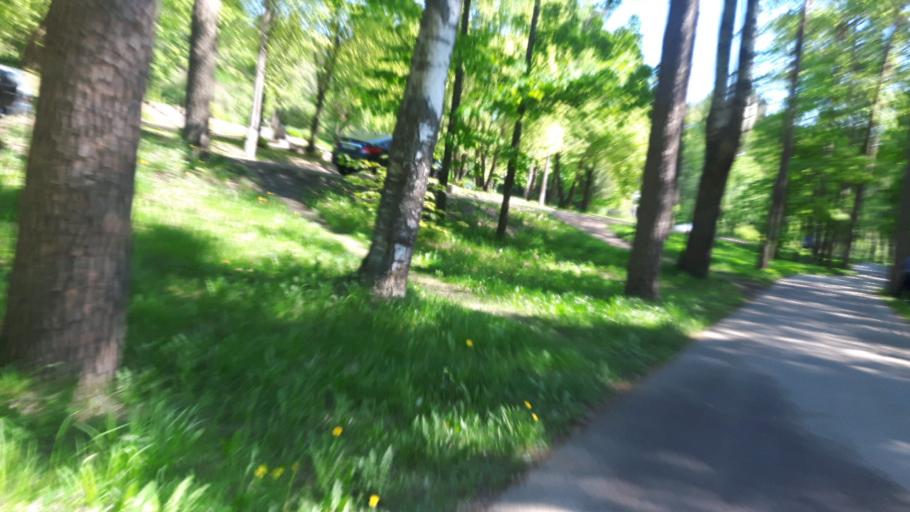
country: RU
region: St.-Petersburg
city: Zelenogorsk
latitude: 60.1919
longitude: 29.7035
